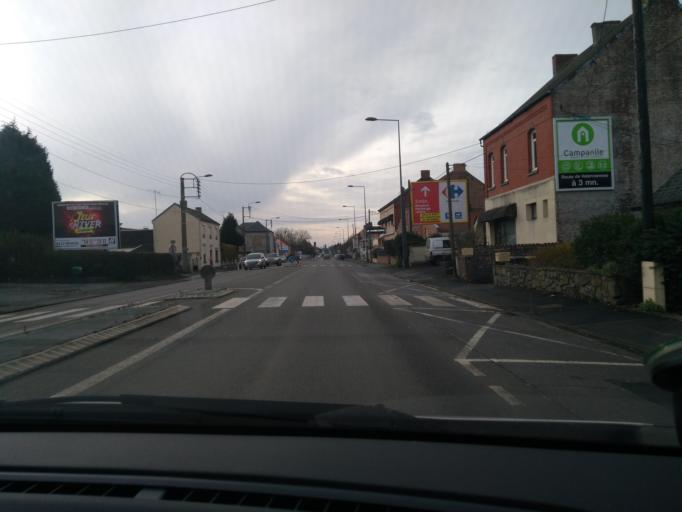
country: FR
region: Nord-Pas-de-Calais
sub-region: Departement du Nord
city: Maubeuge
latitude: 50.2997
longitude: 3.9772
